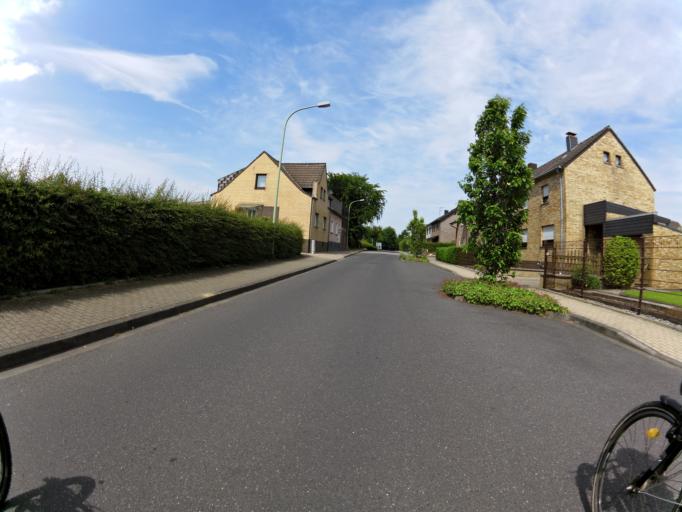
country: DE
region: North Rhine-Westphalia
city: Baesweiler
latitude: 50.9129
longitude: 6.1869
